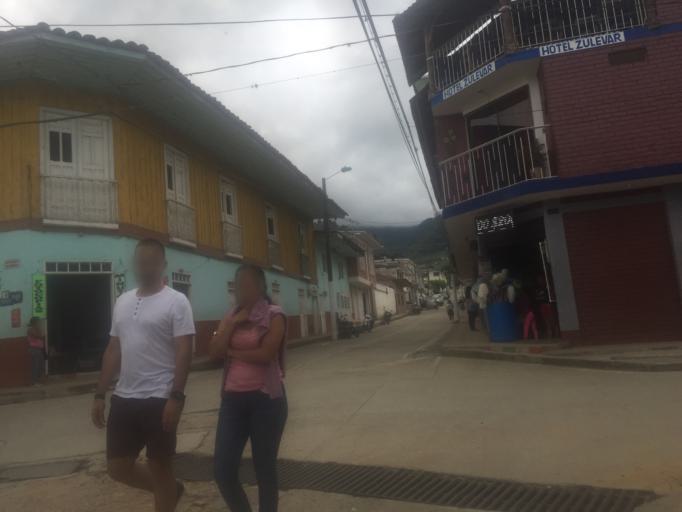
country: CO
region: Valle del Cauca
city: Calimita
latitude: 3.9320
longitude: -76.4852
